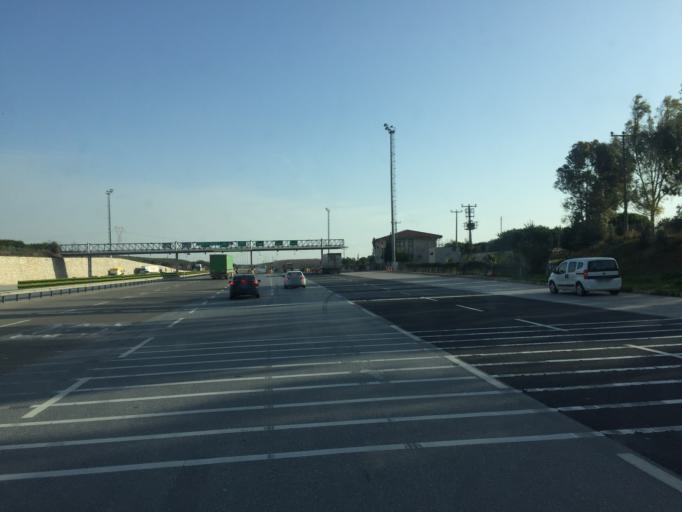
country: TR
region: Mersin
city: Yenice
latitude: 37.0278
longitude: 35.1122
